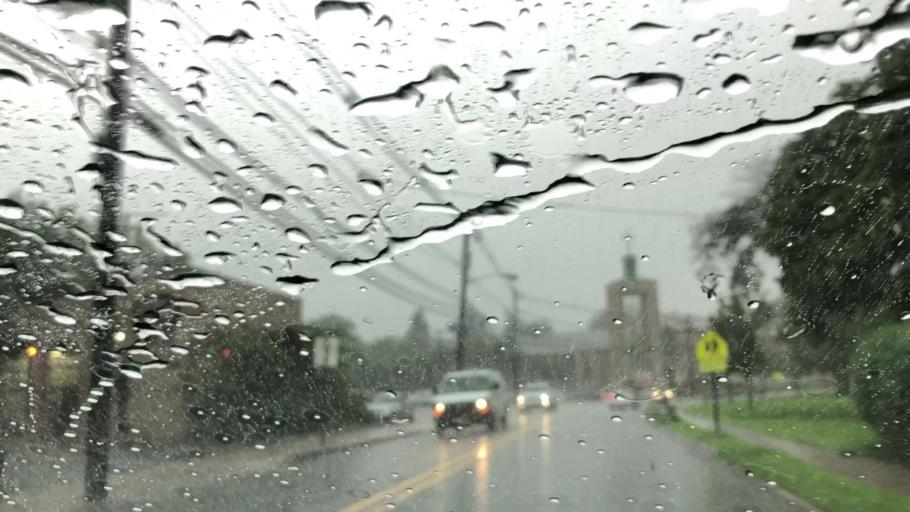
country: US
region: New Jersey
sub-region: Bergen County
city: Rochelle Park
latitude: 40.9041
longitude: -74.0781
